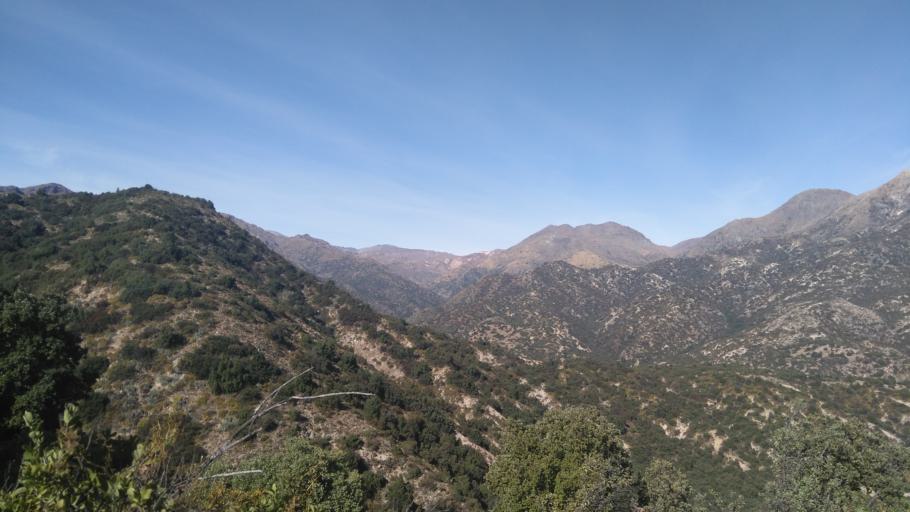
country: CL
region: Santiago Metropolitan
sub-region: Provincia de Cordillera
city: Puente Alto
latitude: -33.7149
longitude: -70.4603
